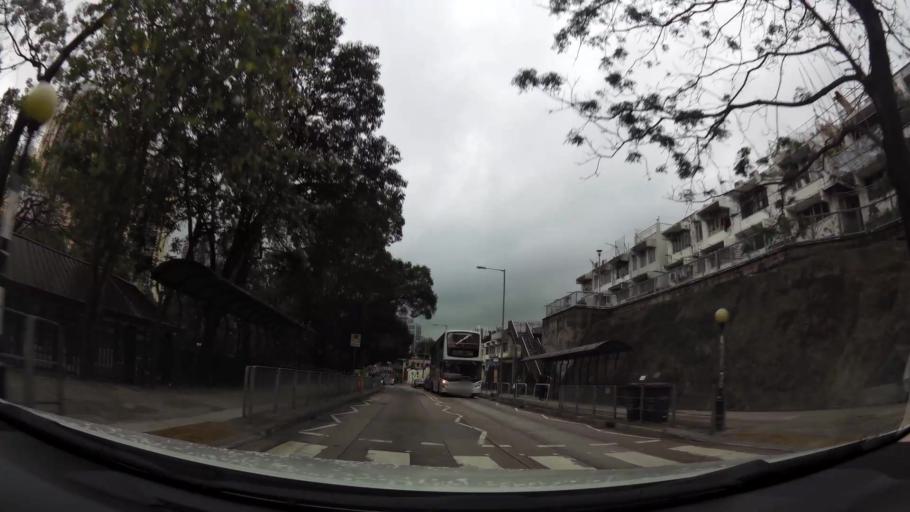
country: HK
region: Tsuen Wan
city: Tsuen Wan
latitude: 22.3717
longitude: 114.1292
